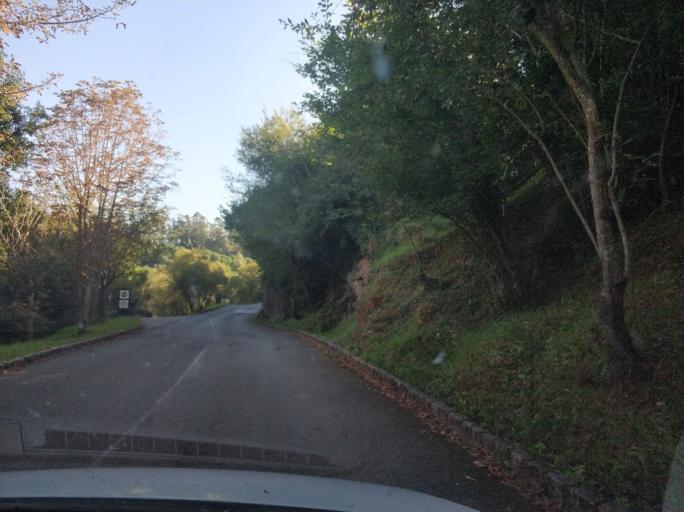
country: ES
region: Cantabria
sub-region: Provincia de Cantabria
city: Penagos
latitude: 43.3489
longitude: -3.8532
